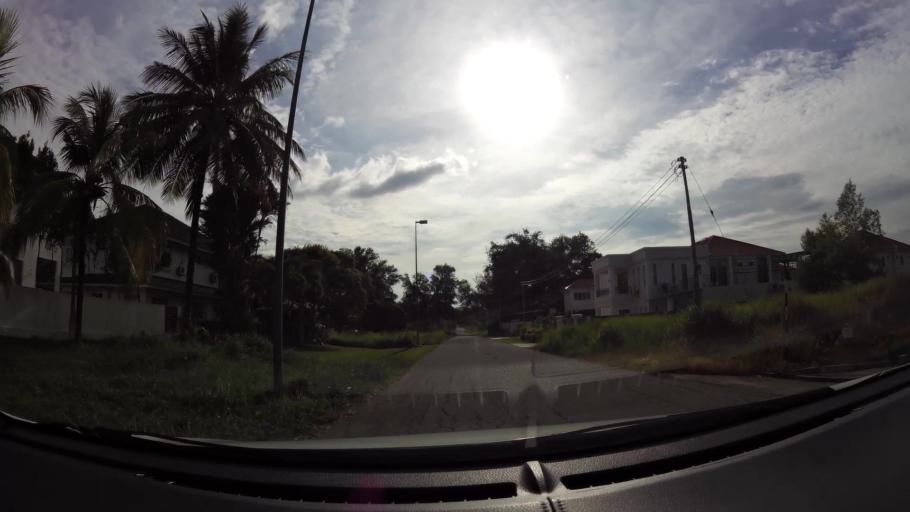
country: BN
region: Brunei and Muara
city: Bandar Seri Begawan
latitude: 4.9098
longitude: 114.8916
